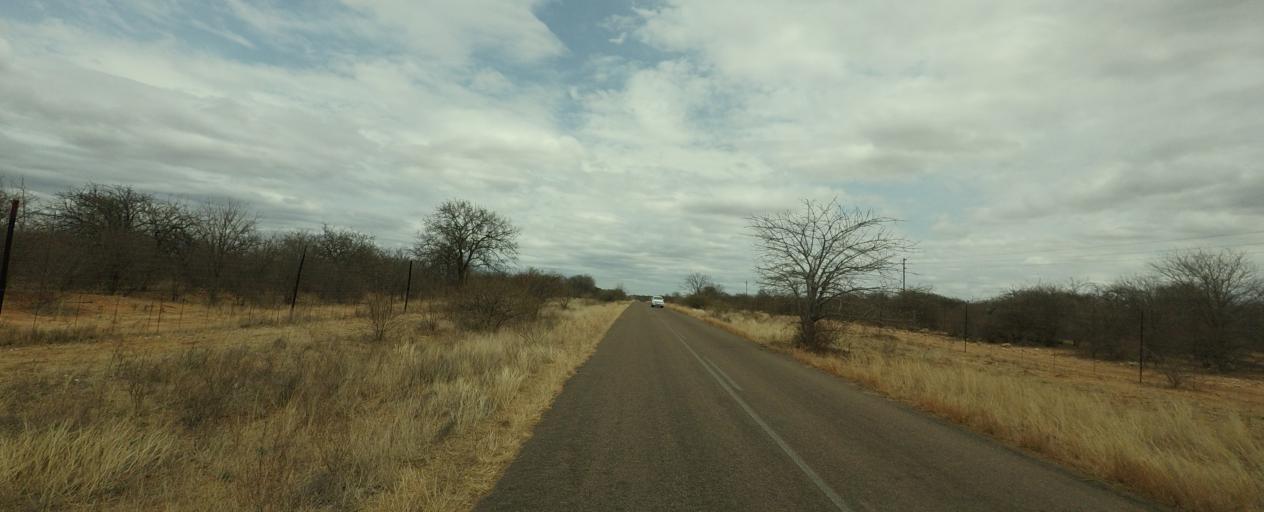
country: BW
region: Central
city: Mathathane
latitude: -22.6651
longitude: 28.6973
